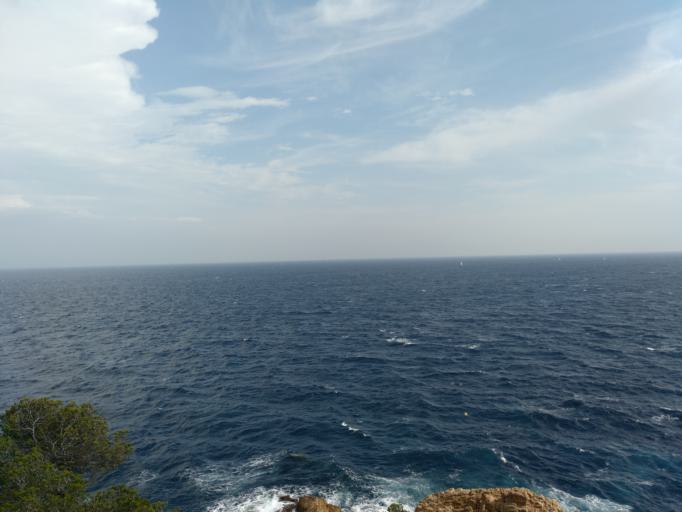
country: ES
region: Catalonia
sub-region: Provincia de Girona
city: Sant Feliu de Guixols
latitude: 41.7724
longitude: 3.0316
